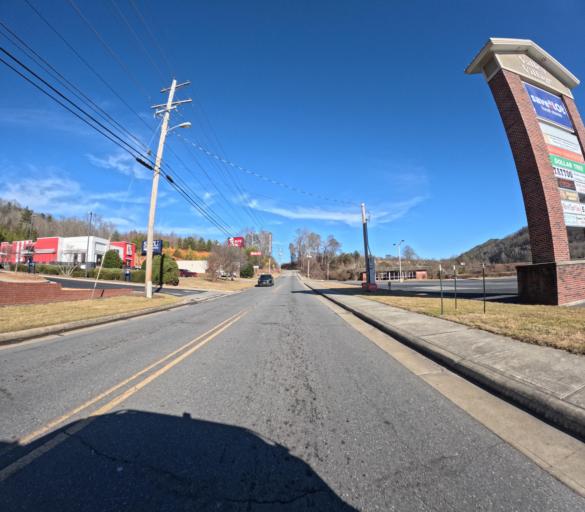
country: US
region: North Carolina
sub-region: Cherokee County
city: Murphy
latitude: 35.1050
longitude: -84.0144
